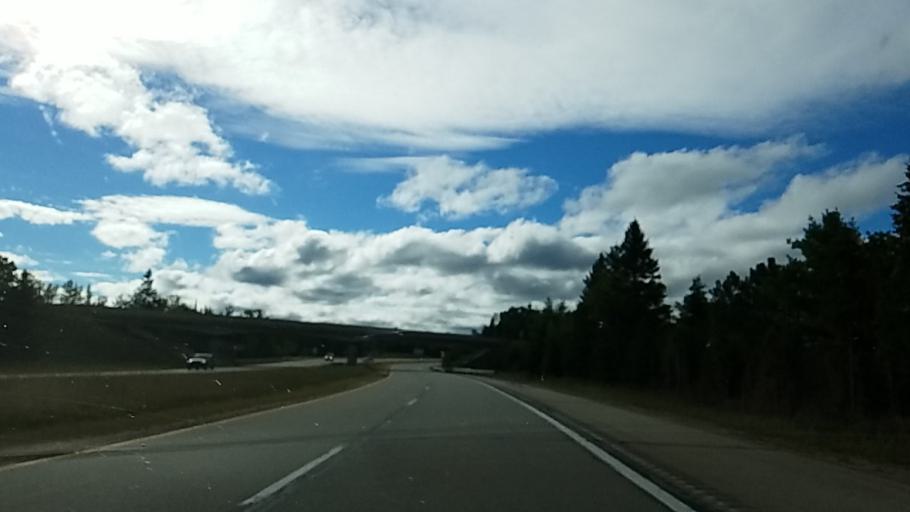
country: US
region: Michigan
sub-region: Mackinac County
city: Saint Ignace
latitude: 45.7637
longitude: -84.7334
